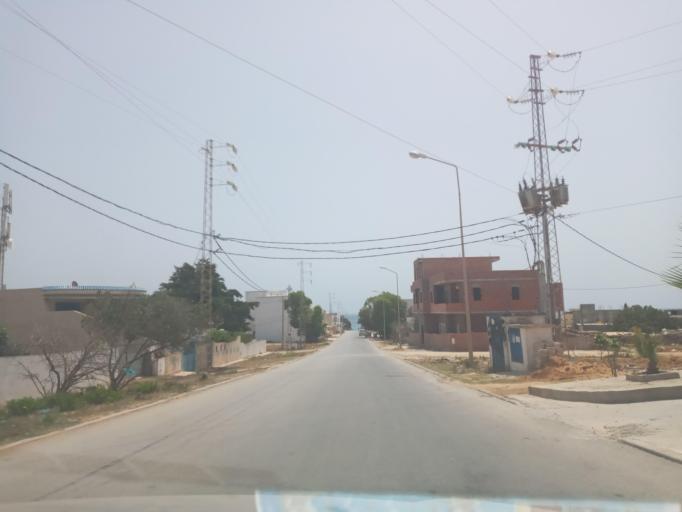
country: TN
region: Nabul
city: El Haouaria
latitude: 37.0370
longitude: 11.0514
